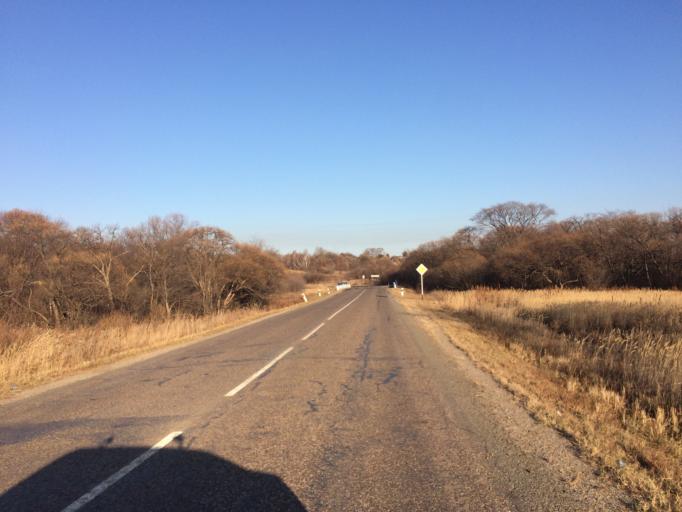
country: RU
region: Primorskiy
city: Ivanovka
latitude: 43.9539
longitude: 132.4611
